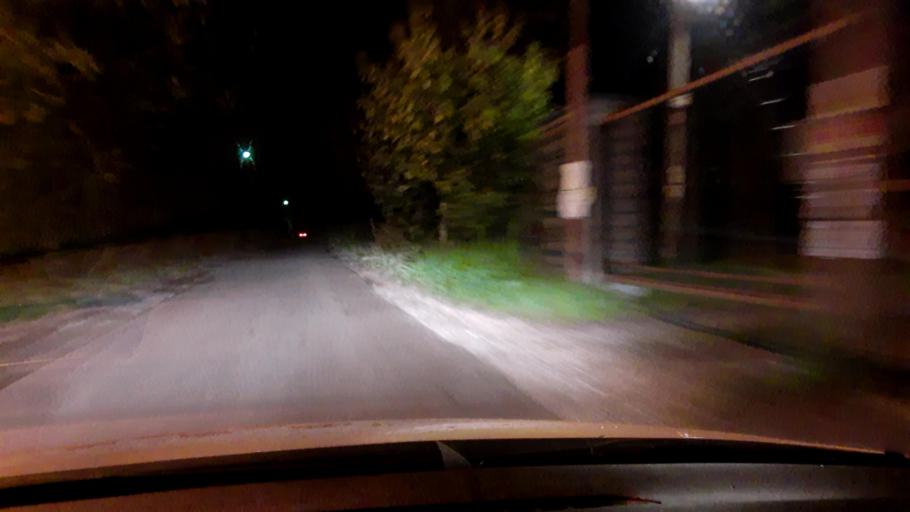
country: RU
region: Moskovskaya
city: Obukhovo
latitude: 55.8040
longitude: 38.3152
